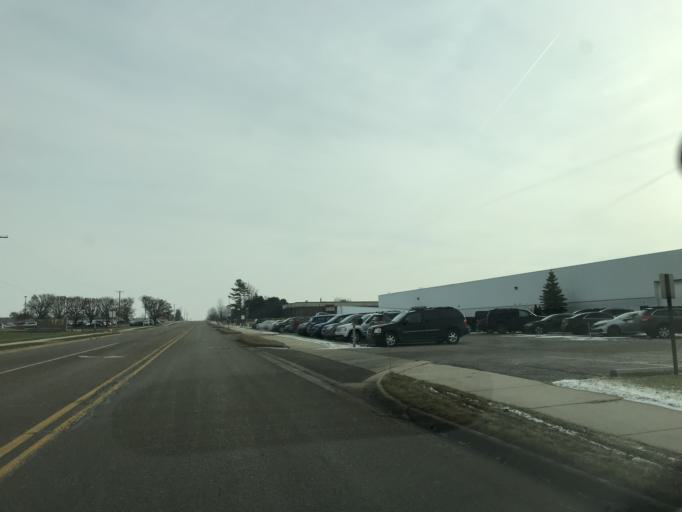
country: US
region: Michigan
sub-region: Ottawa County
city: Holland
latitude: 42.7621
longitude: -86.0771
